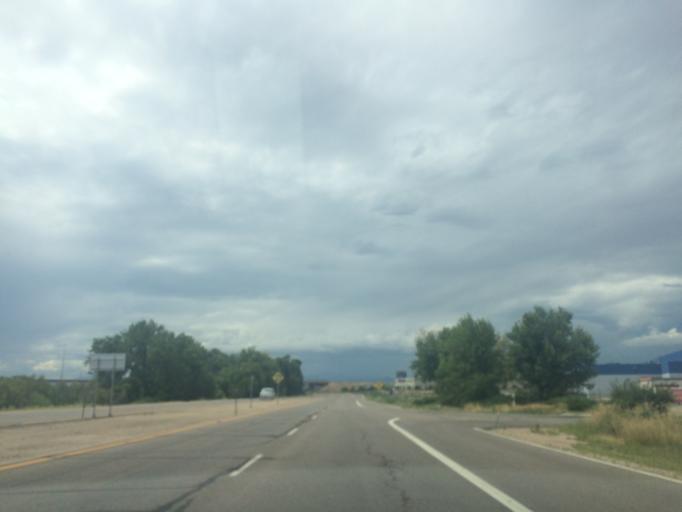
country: US
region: Colorado
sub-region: Adams County
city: Welby
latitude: 39.8288
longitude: -104.9602
